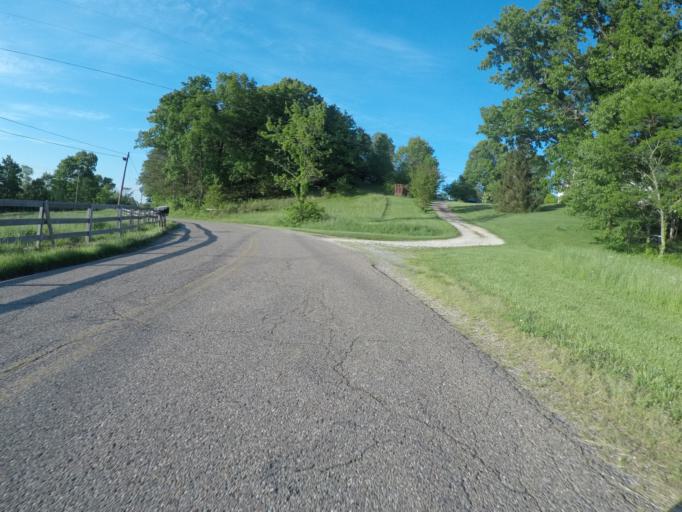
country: US
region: West Virginia
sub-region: Cabell County
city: Huntington
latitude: 38.5488
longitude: -82.4288
